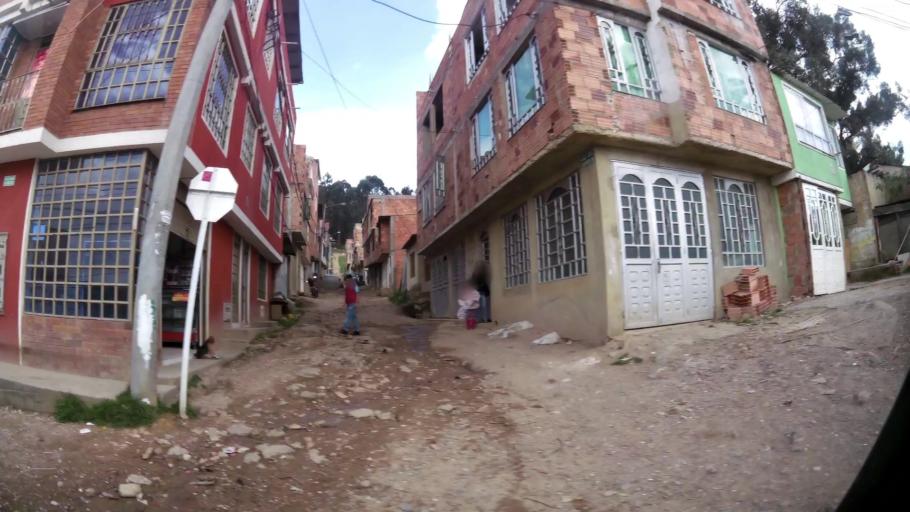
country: CO
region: Bogota D.C.
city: Barrio San Luis
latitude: 4.7322
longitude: -74.0537
